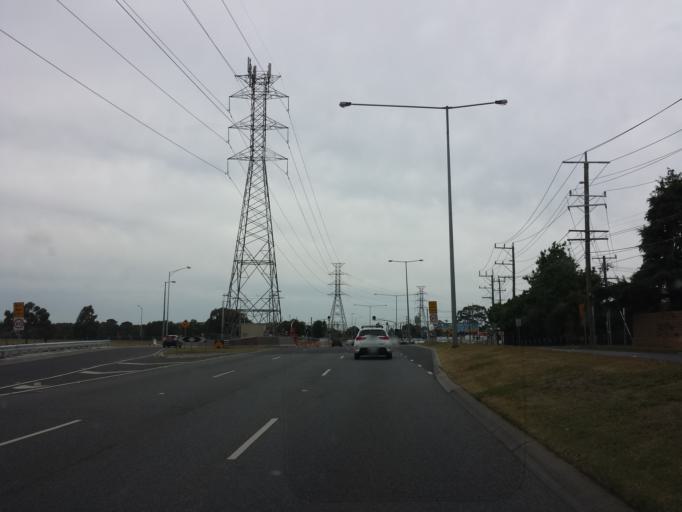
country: AU
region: Victoria
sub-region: Monash
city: Oakleigh South
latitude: -37.9372
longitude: 145.0799
